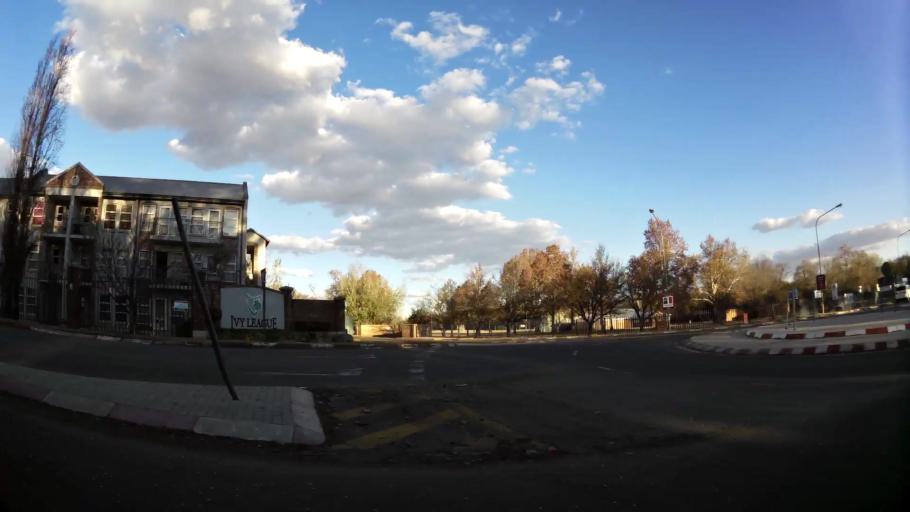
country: ZA
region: North-West
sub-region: Dr Kenneth Kaunda District Municipality
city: Potchefstroom
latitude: -26.6835
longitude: 27.1015
